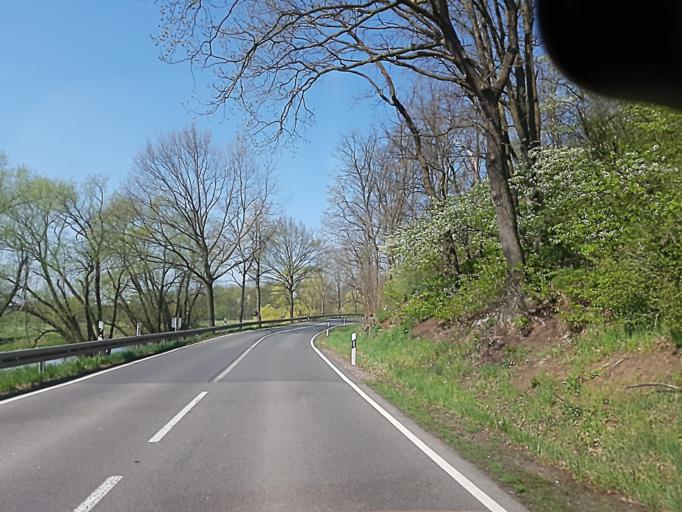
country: DE
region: Saxony
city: Leisnig
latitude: 51.1766
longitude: 12.9118
